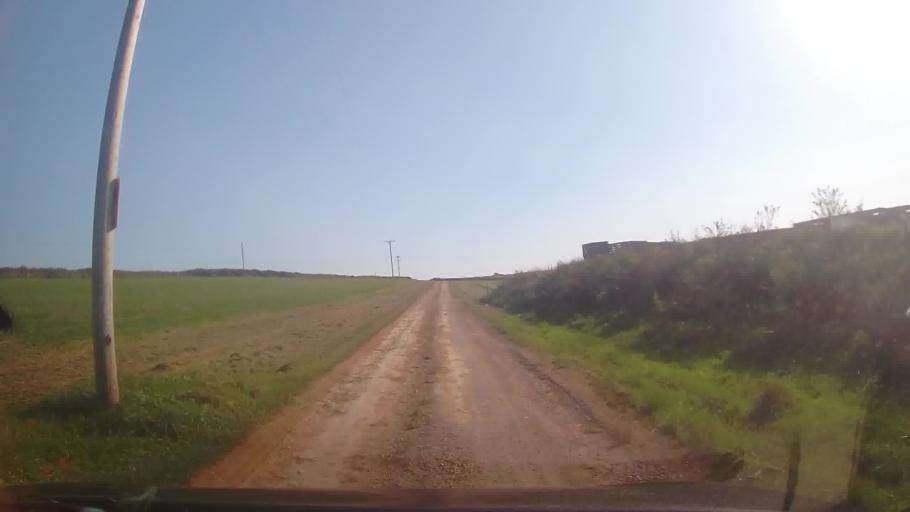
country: GB
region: Wales
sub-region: Pembrokeshire
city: Llanrhian
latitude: 51.9251
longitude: -5.2194
